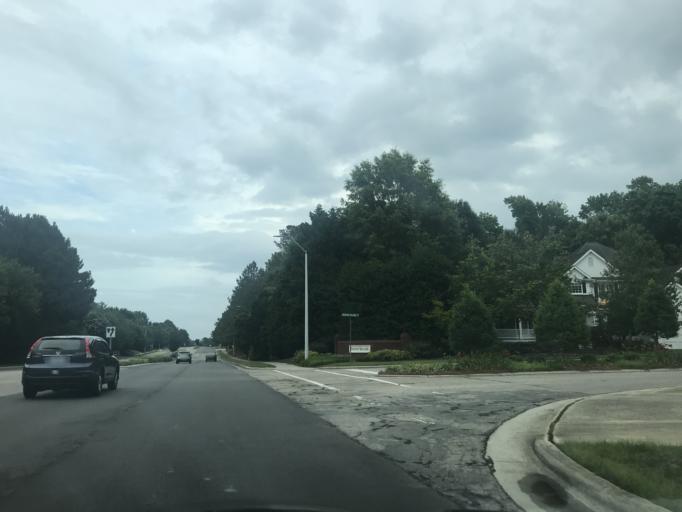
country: US
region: North Carolina
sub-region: Wake County
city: Morrisville
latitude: 35.8135
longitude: -78.8600
